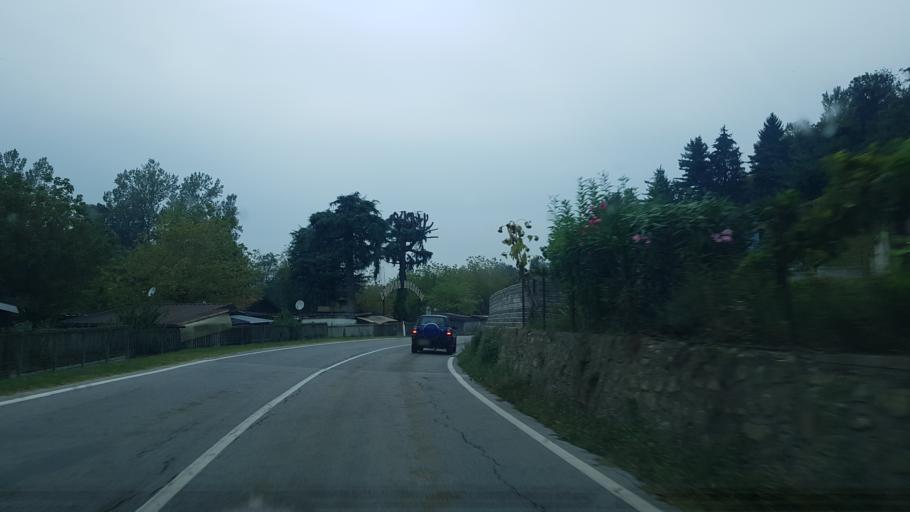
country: IT
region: Piedmont
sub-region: Provincia di Cuneo
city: Frabosa Sottana
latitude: 44.3241
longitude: 7.8010
